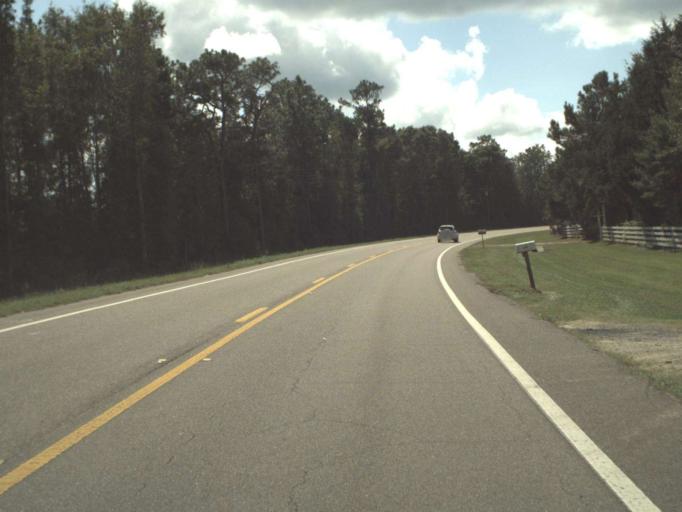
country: US
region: Florida
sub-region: Walton County
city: Freeport
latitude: 30.4999
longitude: -85.9285
